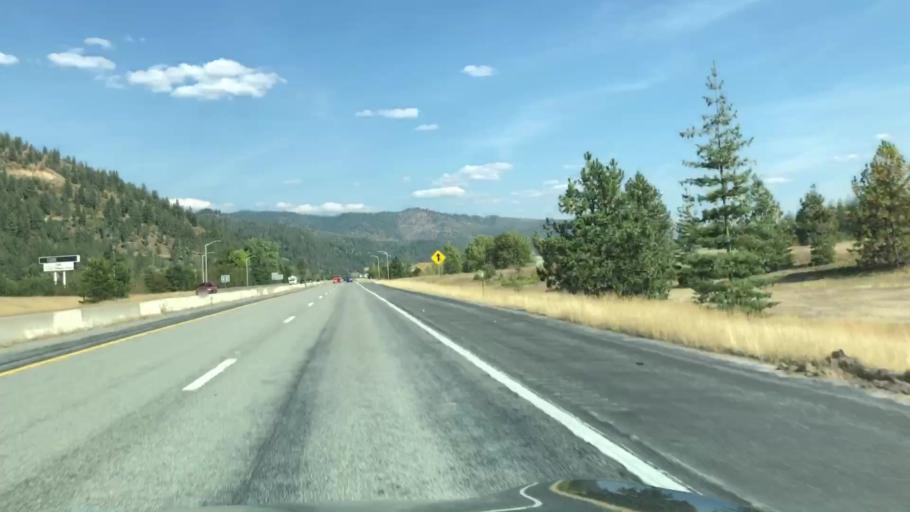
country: US
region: Idaho
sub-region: Shoshone County
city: Kellogg
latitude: 47.5466
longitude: -116.1746
